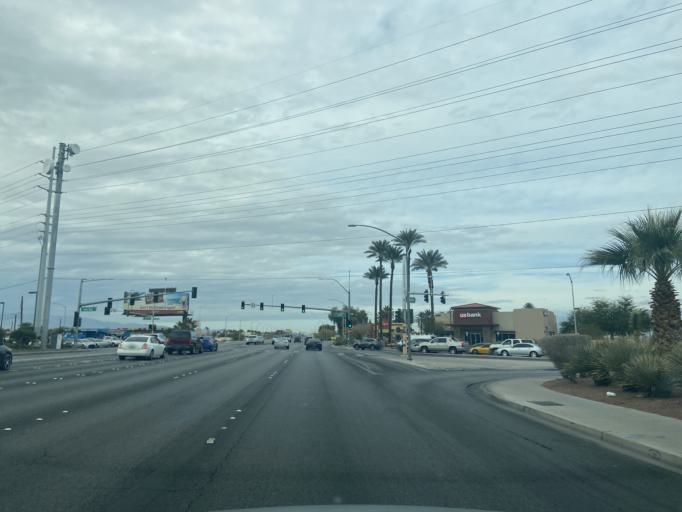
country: US
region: Nevada
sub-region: Clark County
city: Las Vegas
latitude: 36.2023
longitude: -115.1984
